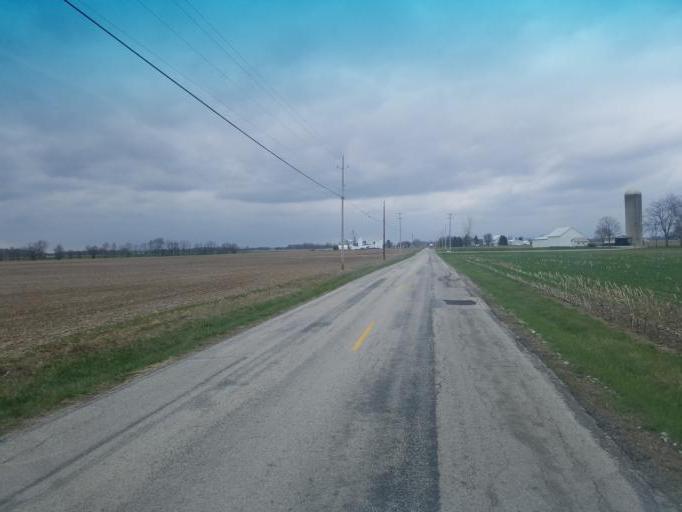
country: US
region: Ohio
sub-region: Marion County
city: Prospect
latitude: 40.4587
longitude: -83.1548
